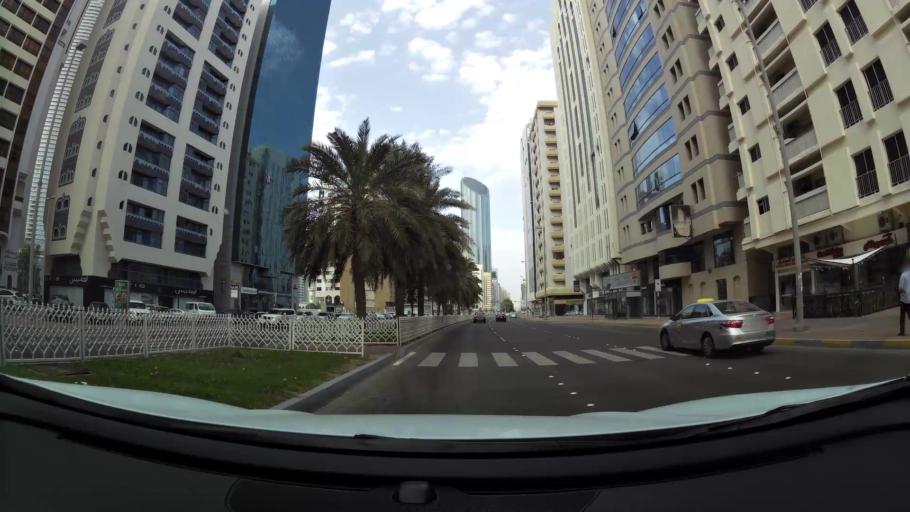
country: AE
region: Abu Dhabi
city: Abu Dhabi
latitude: 24.4814
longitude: 54.3516
